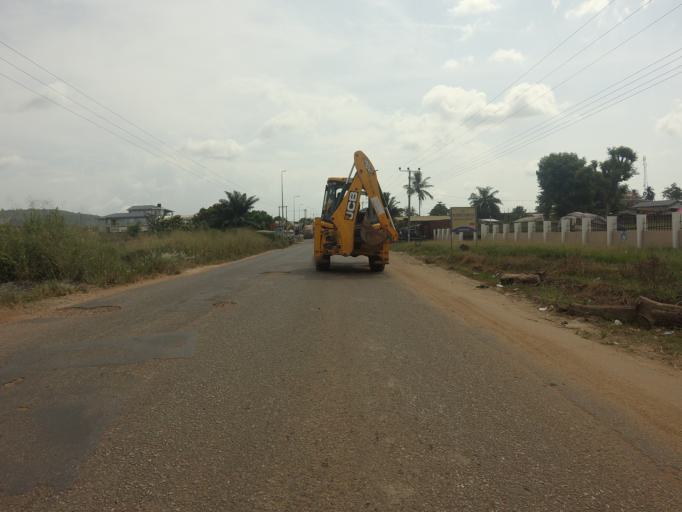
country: GH
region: Eastern
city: Koforidua
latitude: 6.0409
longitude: -0.2605
